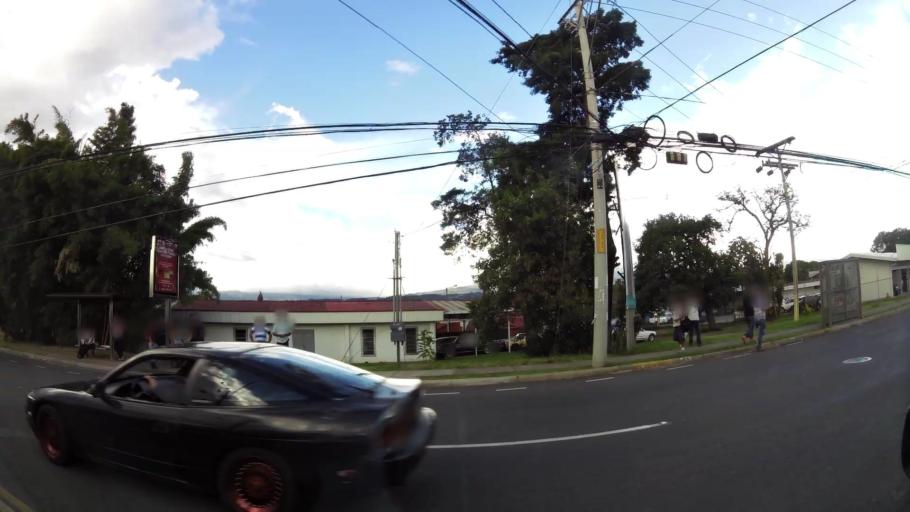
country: CR
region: Alajuela
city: Alajuela
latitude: 10.0012
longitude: -84.1994
